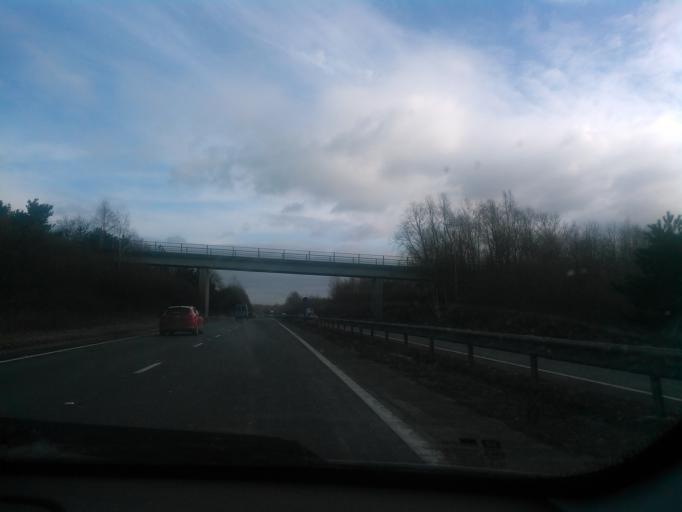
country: GB
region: England
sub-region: Derbyshire
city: Etwall
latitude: 52.8790
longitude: -1.6582
